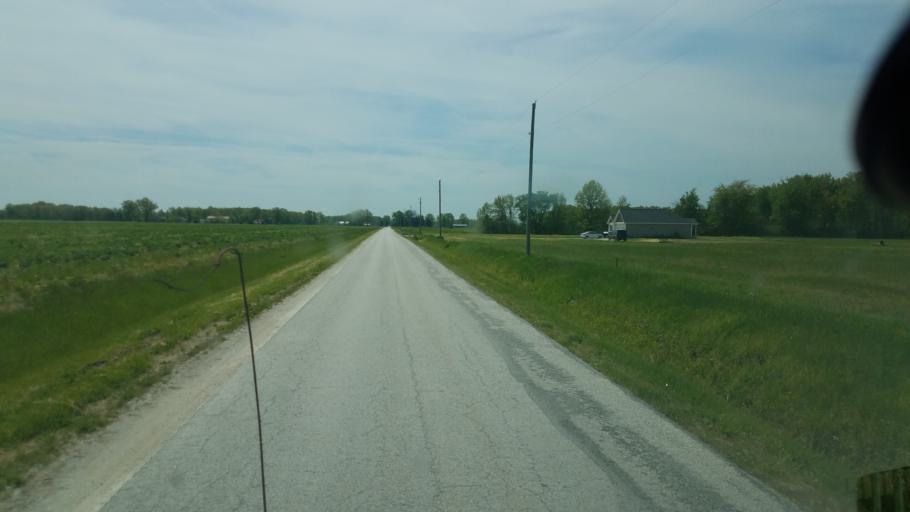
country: US
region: Ohio
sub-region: Ottawa County
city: Oak Harbor
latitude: 41.4927
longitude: -83.1642
